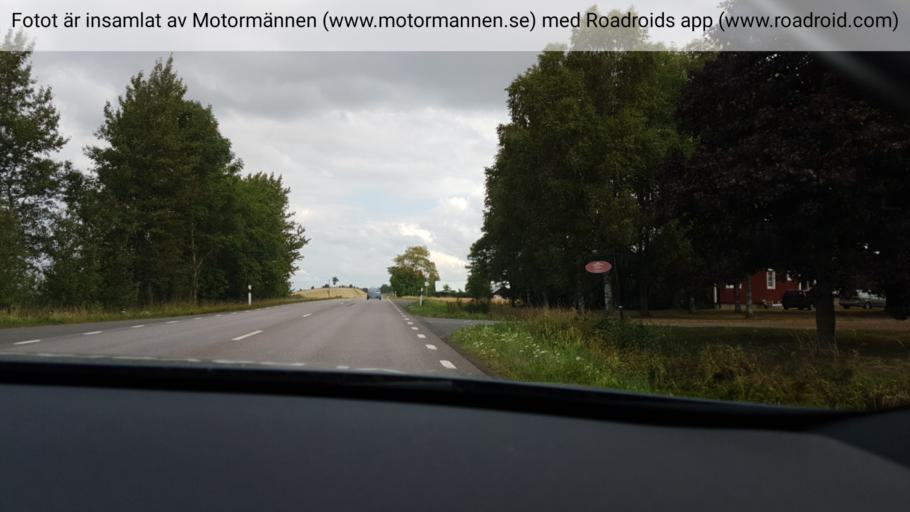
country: SE
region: Vaestra Goetaland
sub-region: Falkopings Kommun
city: Falkoeping
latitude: 58.1244
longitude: 13.5503
